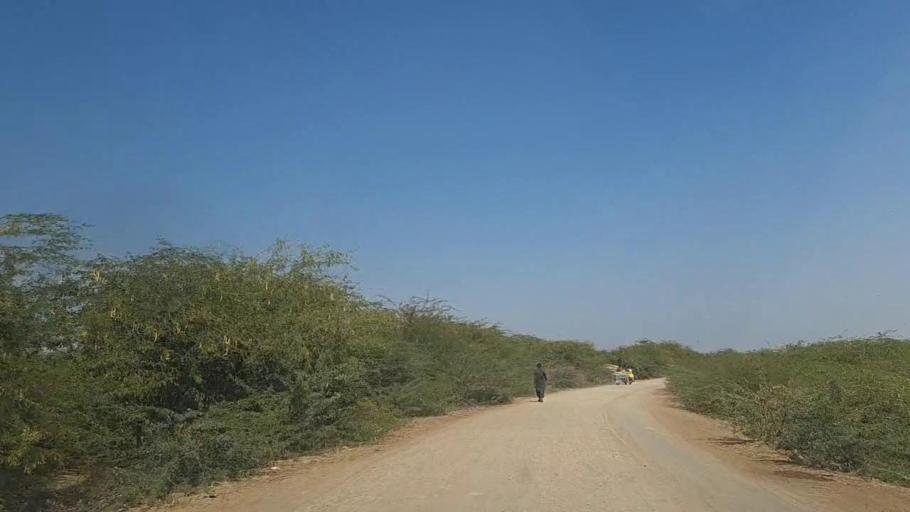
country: PK
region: Sindh
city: Digri
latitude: 25.1702
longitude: 69.1998
